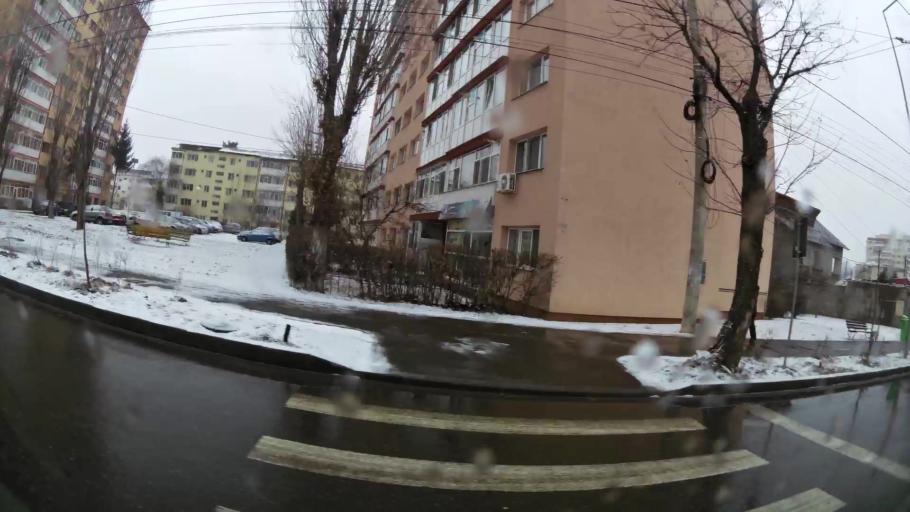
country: RO
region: Dambovita
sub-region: Municipiul Targoviste
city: Targoviste
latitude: 44.9258
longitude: 25.4402
